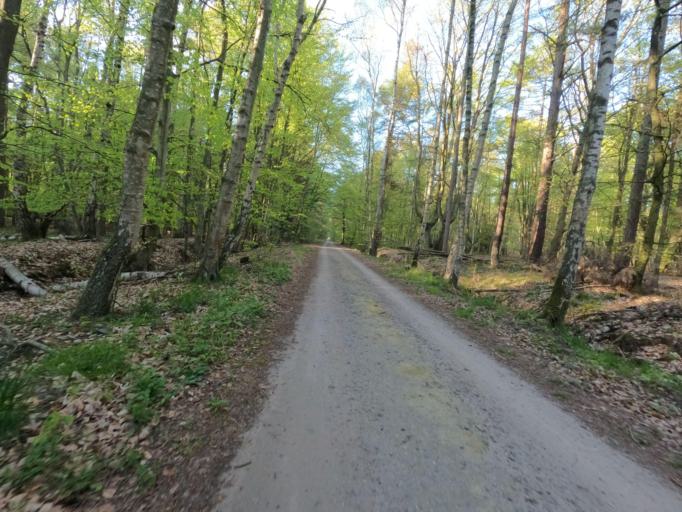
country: DE
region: Mecklenburg-Vorpommern
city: Born
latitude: 54.4252
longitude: 12.5366
